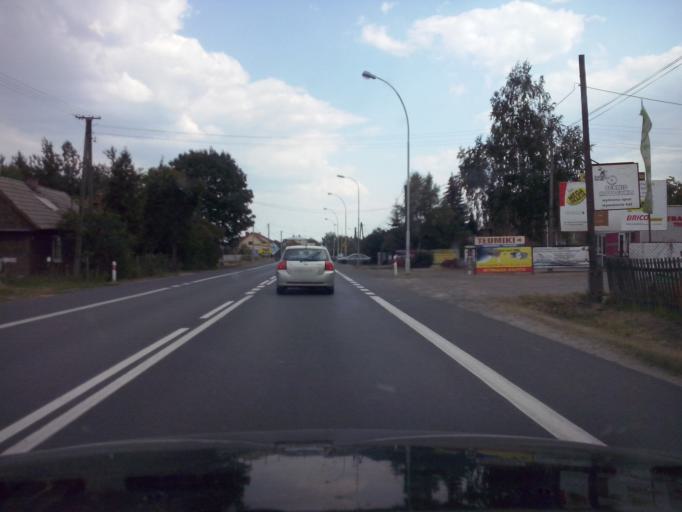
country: PL
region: Subcarpathian Voivodeship
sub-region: Powiat stalowowolski
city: Pysznica
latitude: 50.5391
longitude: 22.0973
